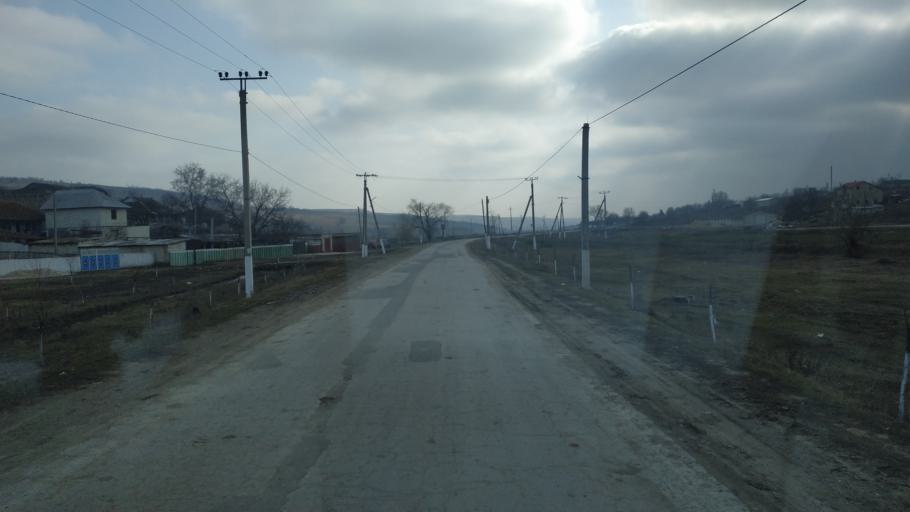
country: MD
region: Nisporeni
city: Nisporeni
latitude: 46.9366
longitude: 28.3284
